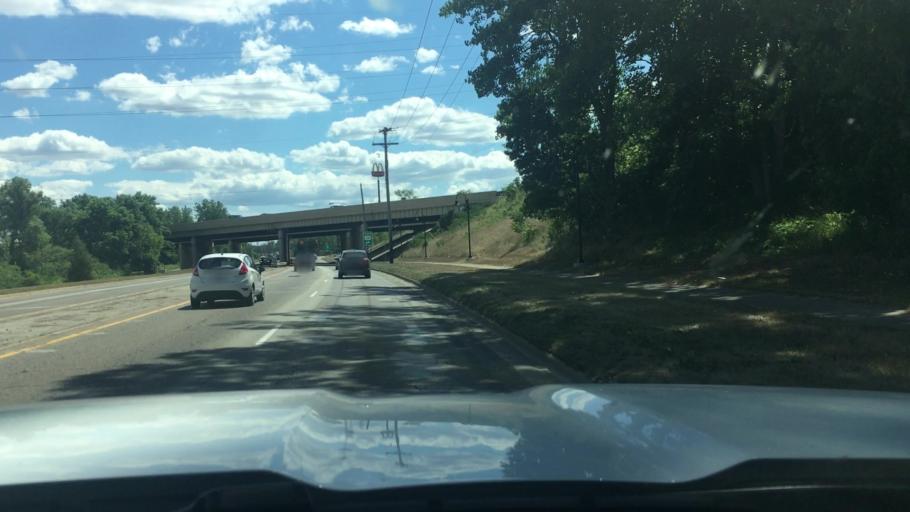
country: US
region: Michigan
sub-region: Kent County
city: Comstock Park
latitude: 43.0423
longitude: -85.6607
